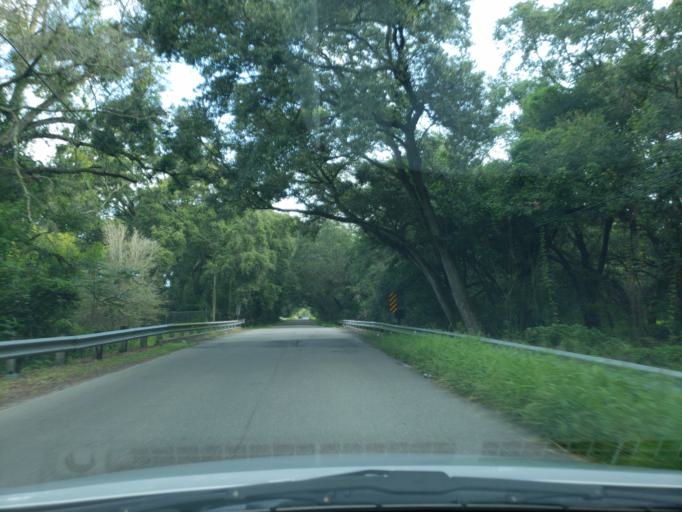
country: US
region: Florida
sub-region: Hillsborough County
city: Palm River-Clair Mel
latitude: 27.9277
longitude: -82.3606
